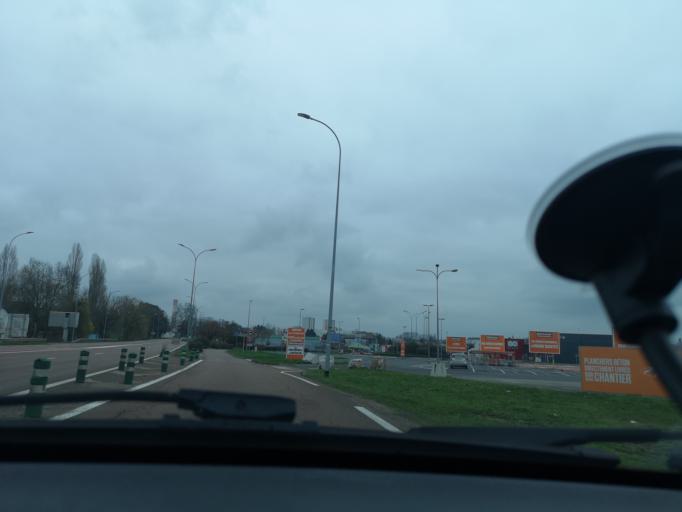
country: FR
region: Bourgogne
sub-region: Departement de Saone-et-Loire
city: Champforgeuil
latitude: 46.7993
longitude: 4.8340
